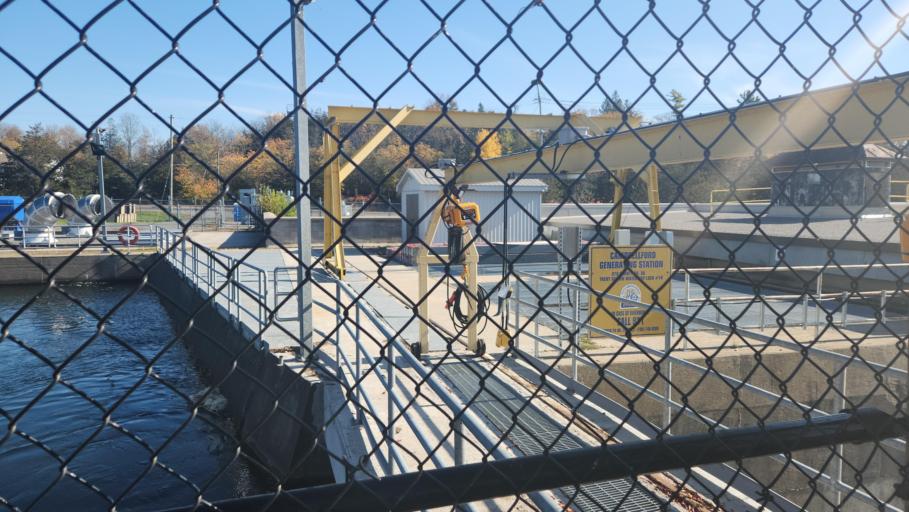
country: CA
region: Ontario
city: Quinte West
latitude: 44.3352
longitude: -77.7727
